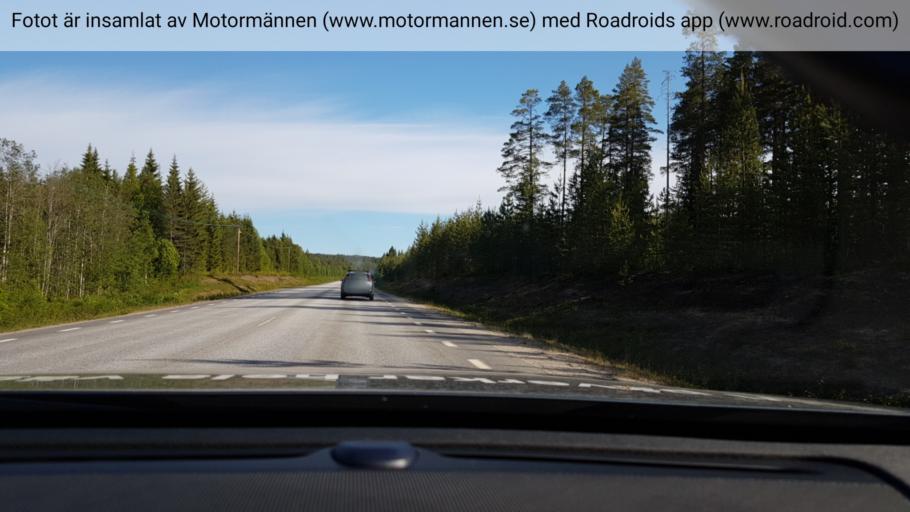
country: SE
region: Vaesterbotten
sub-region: Vannas Kommun
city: Vaennaes
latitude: 64.0150
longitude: 19.6937
